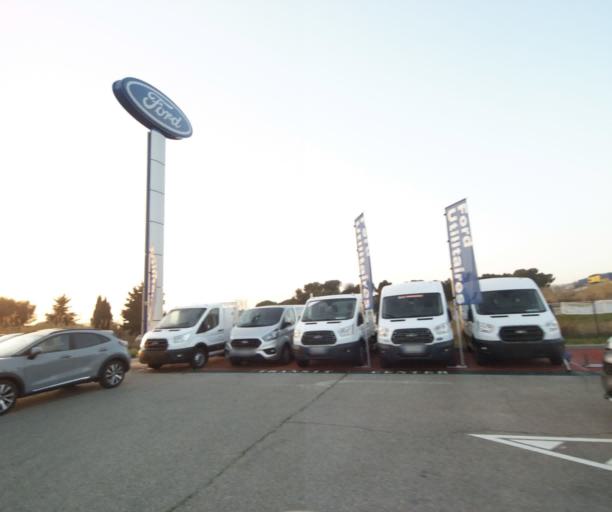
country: FR
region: Provence-Alpes-Cote d'Azur
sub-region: Departement des Bouches-du-Rhone
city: Saint-Victoret
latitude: 43.4270
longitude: 5.2669
